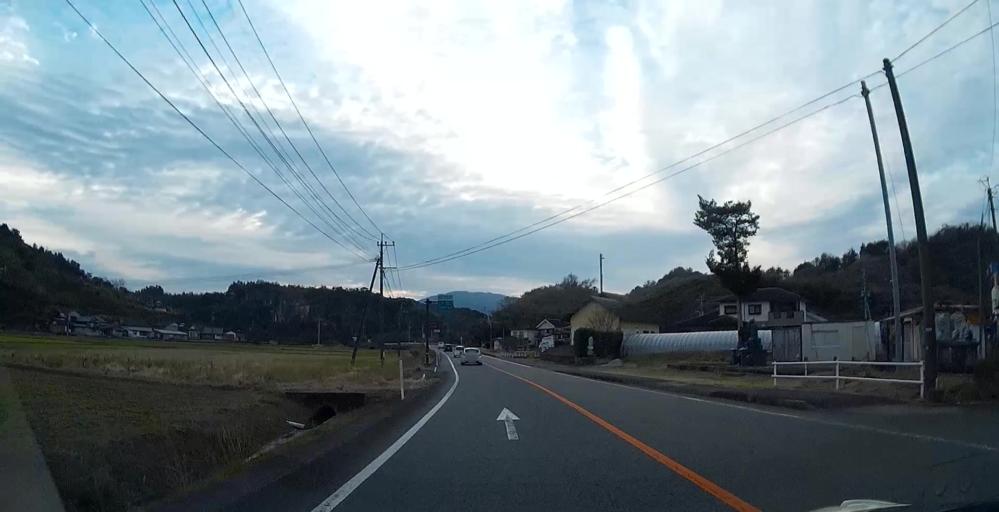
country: JP
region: Kumamoto
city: Yatsushiro
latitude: 32.5004
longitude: 130.4011
